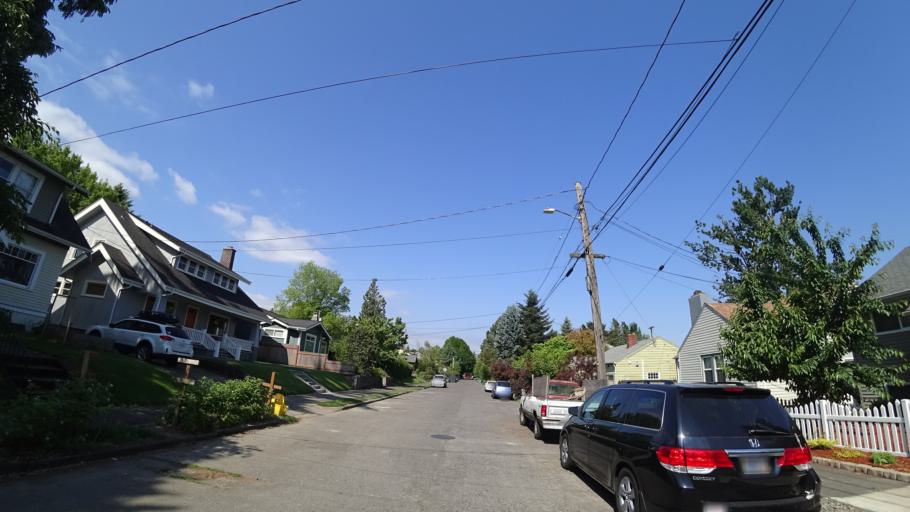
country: US
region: Oregon
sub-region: Multnomah County
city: Portland
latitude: 45.5725
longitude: -122.6475
